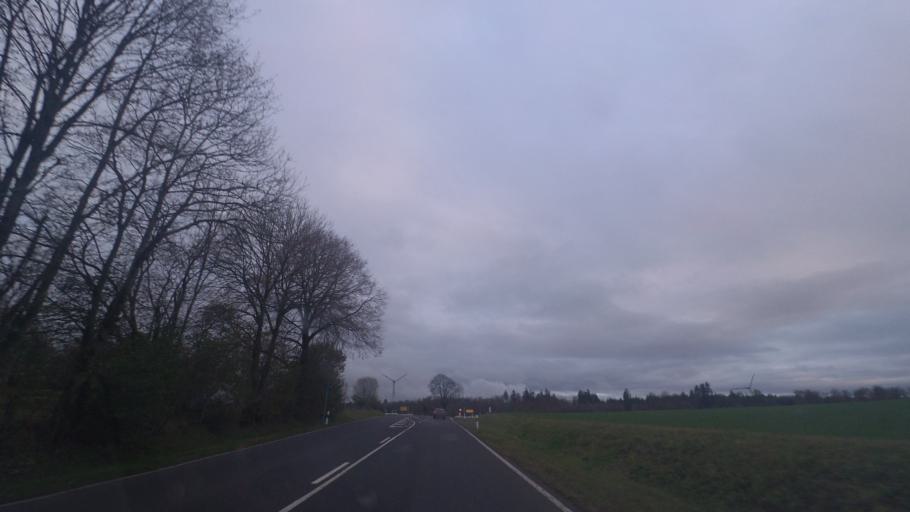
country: DE
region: Hesse
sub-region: Regierungsbezirk Giessen
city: Freiensteinau
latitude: 50.4582
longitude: 9.3917
